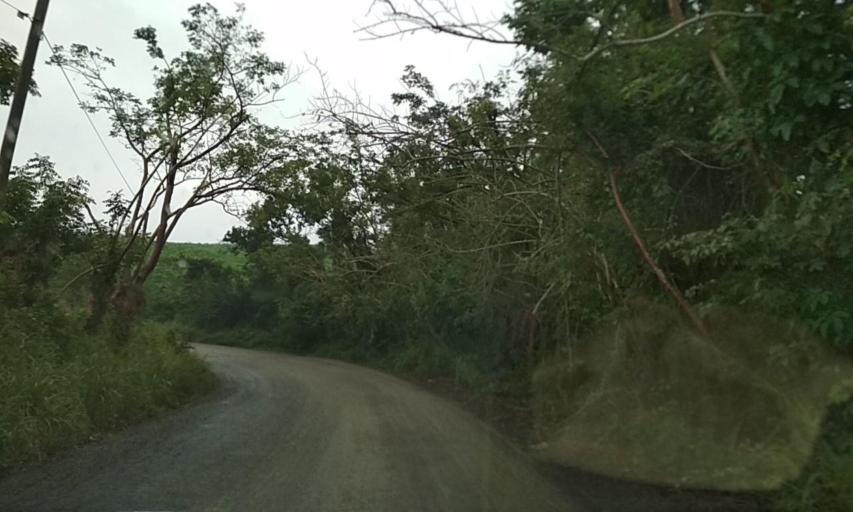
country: MX
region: Veracruz
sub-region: Coatzintla
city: Manuel Maria Contreras
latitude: 20.4594
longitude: -97.4738
